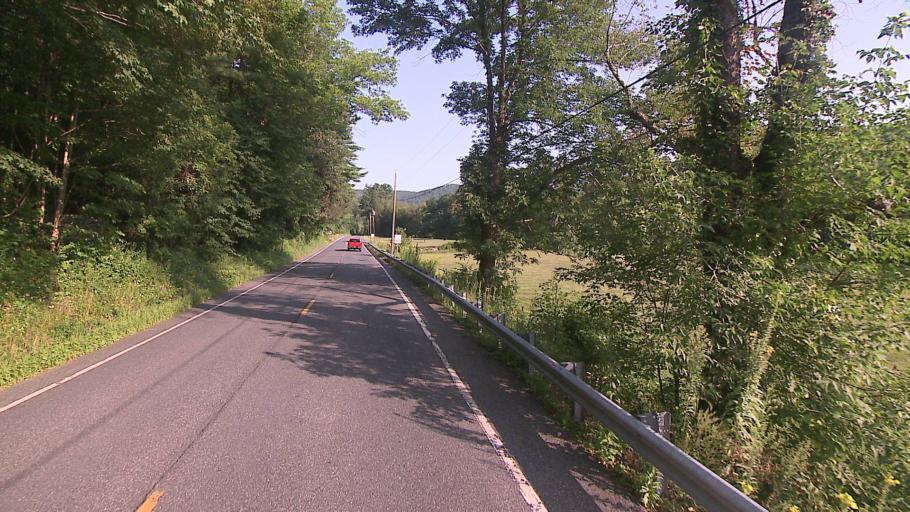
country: US
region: Connecticut
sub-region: Litchfield County
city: Kent
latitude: 41.8232
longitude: -73.3774
